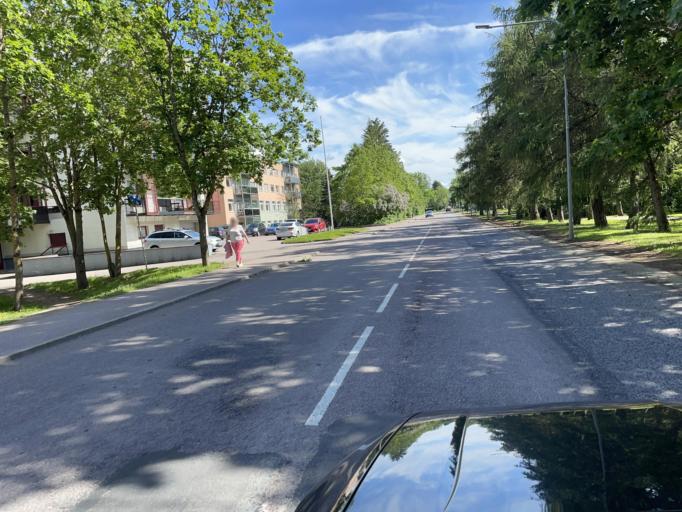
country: EE
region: Harju
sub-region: Keila linn
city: Keila
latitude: 59.3125
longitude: 24.4146
